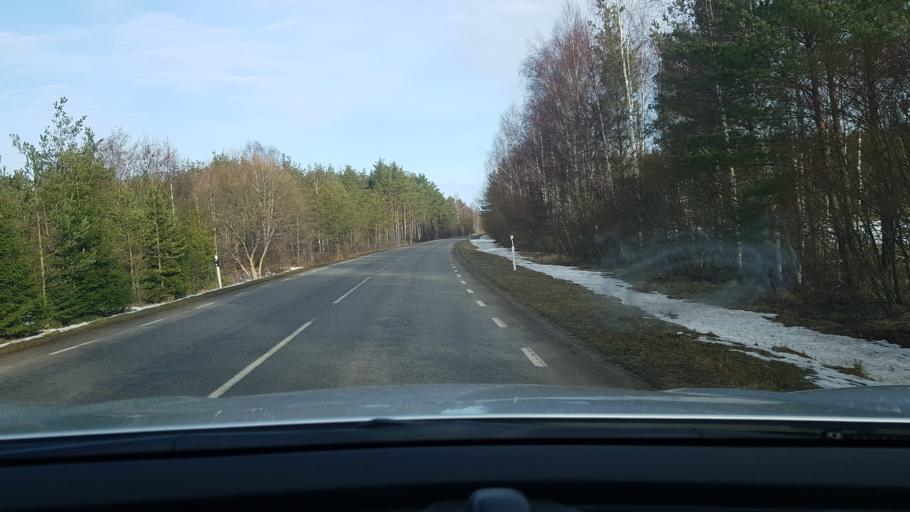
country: EE
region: Saare
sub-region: Kuressaare linn
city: Kuressaare
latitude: 58.4790
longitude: 22.7038
